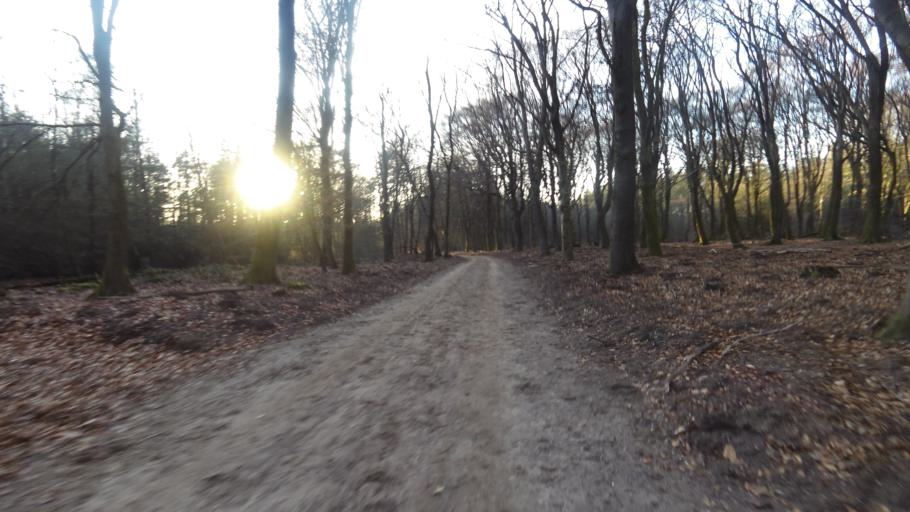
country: NL
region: Gelderland
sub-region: Gemeente Putten
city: Putten
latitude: 52.2480
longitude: 5.6507
